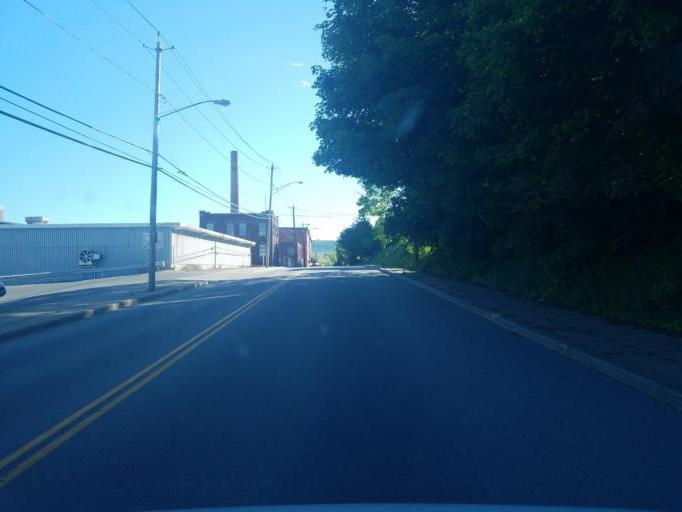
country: US
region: New York
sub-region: Herkimer County
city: Little Falls
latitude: 43.0337
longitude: -74.8720
